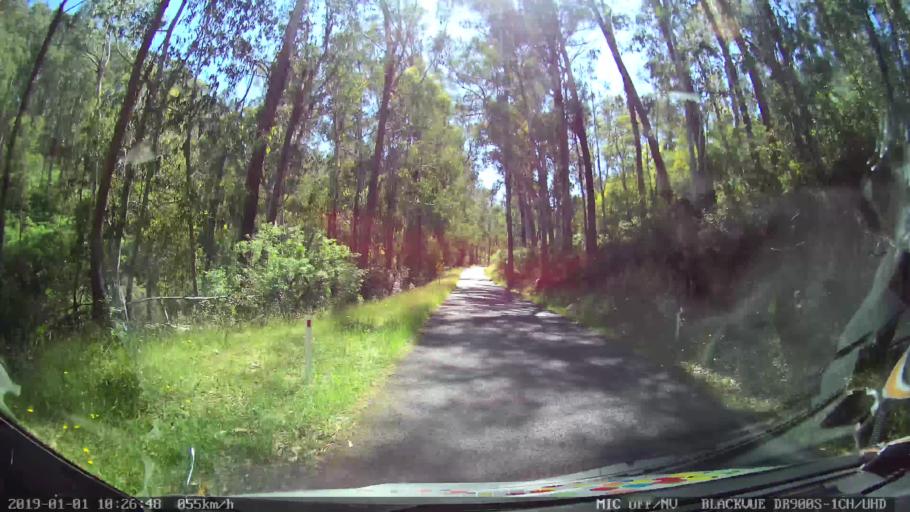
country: AU
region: New South Wales
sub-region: Snowy River
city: Jindabyne
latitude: -36.0668
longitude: 148.2312
